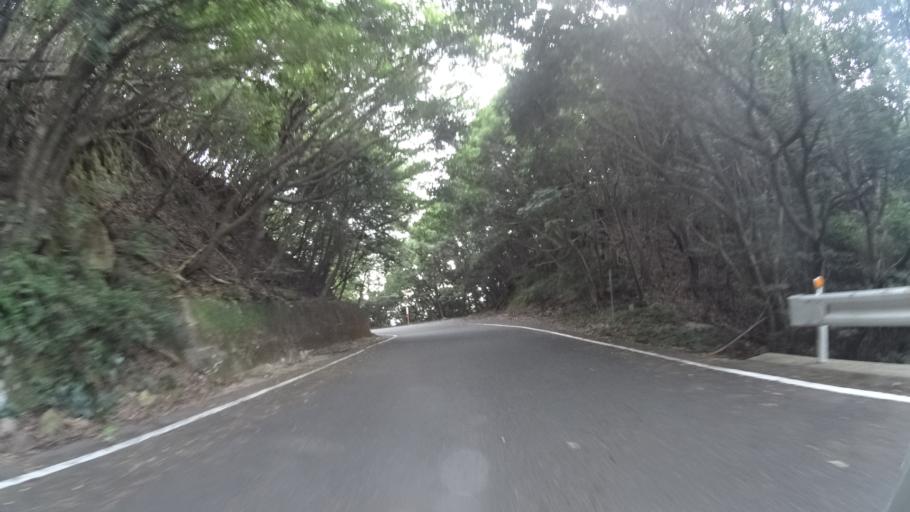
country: JP
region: Kagoshima
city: Nishinoomote
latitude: 30.3356
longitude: 130.3956
